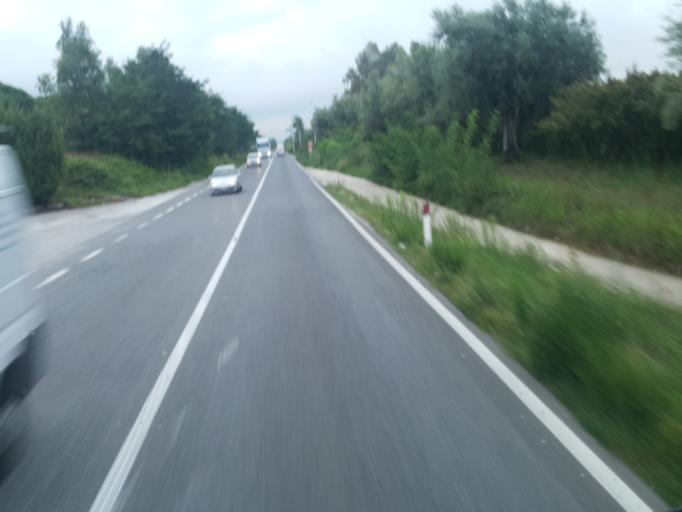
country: IT
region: Campania
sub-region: Provincia di Caserta
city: Pignataro Maggiore
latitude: 41.1709
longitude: 14.1416
